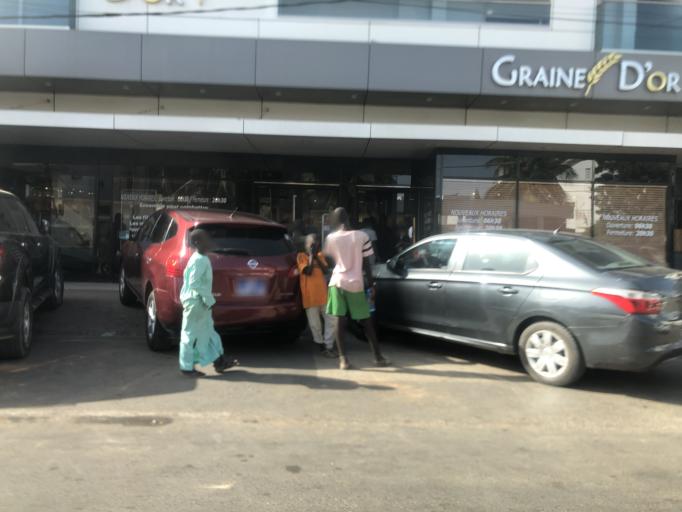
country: SN
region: Dakar
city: Mermoz Boabab
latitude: 14.7494
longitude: -17.5059
